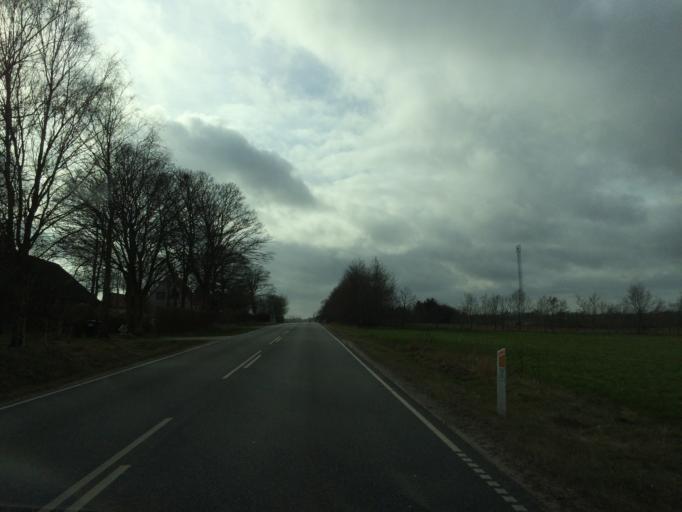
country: DK
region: Central Jutland
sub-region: Favrskov Kommune
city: Ulstrup
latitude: 56.4958
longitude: 9.8159
